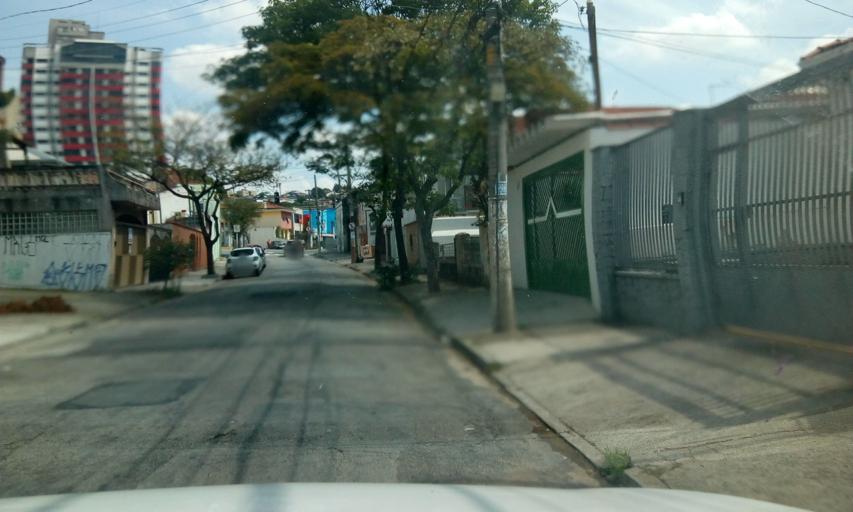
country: BR
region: Sao Paulo
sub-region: Sao Paulo
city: Sao Paulo
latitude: -23.5270
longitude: -46.7042
